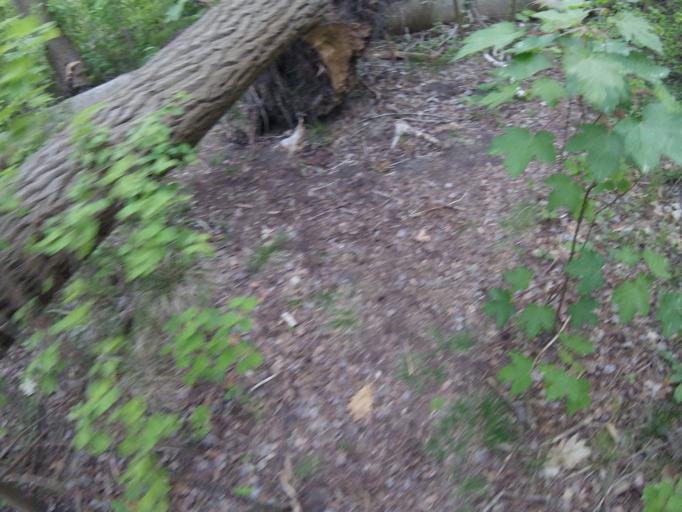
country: DE
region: Brandenburg
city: Bestensee
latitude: 52.2520
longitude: 13.6659
